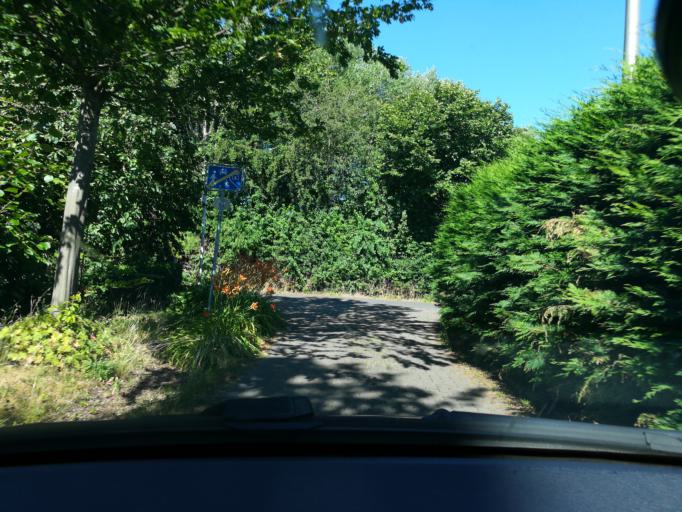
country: DE
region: North Rhine-Westphalia
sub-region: Regierungsbezirk Detmold
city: Minden
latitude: 52.3096
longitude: 8.9390
